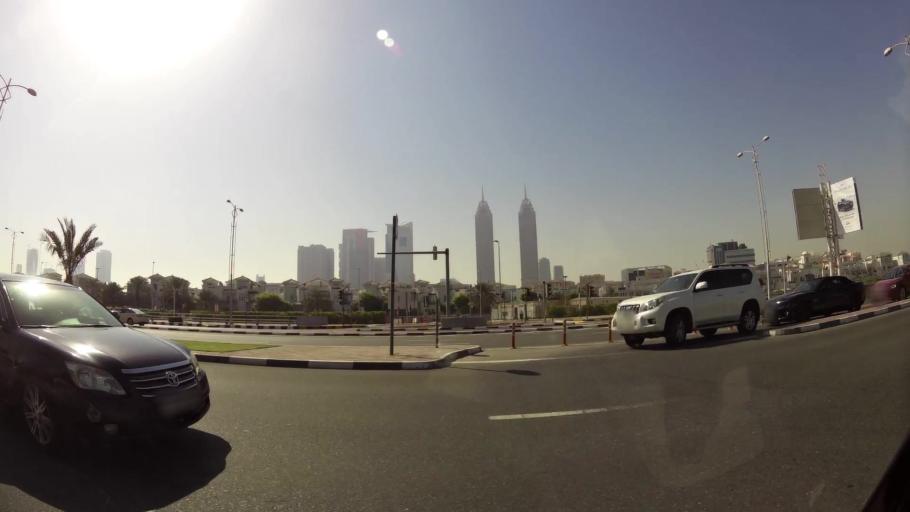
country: AE
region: Dubai
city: Dubai
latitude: 25.1062
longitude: 55.1628
